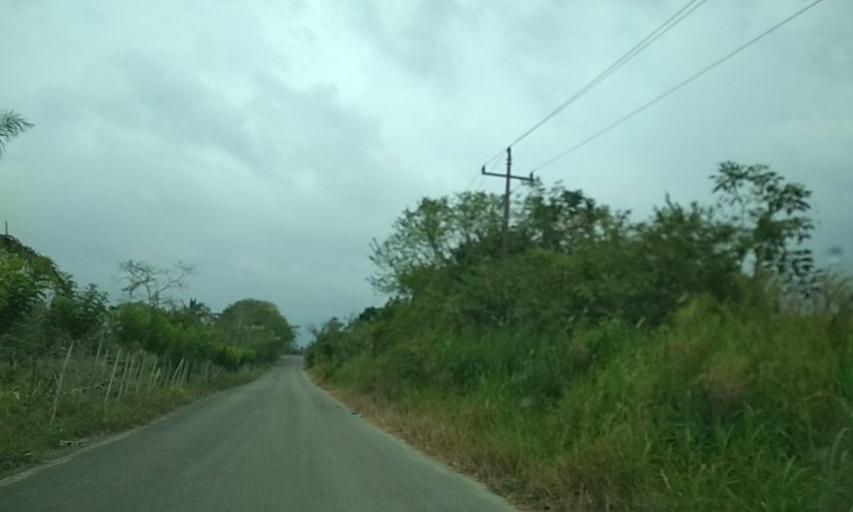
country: MX
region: Tabasco
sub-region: Huimanguillo
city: Francisco Rueda
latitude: 17.6018
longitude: -94.0908
